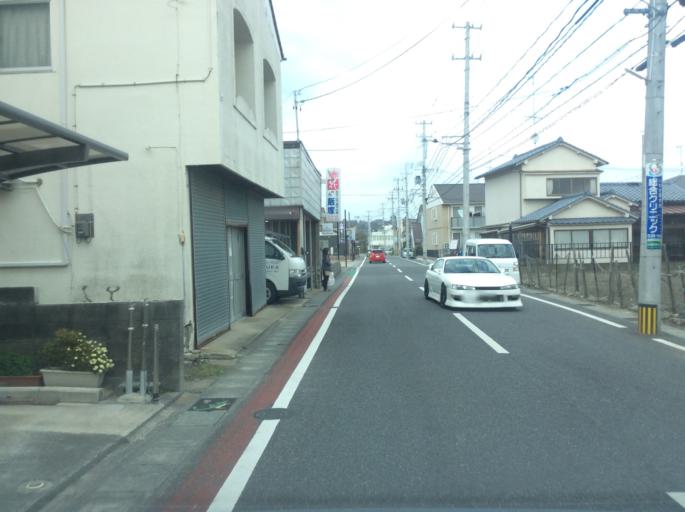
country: JP
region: Fukushima
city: Iwaki
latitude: 37.1034
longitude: 140.9840
